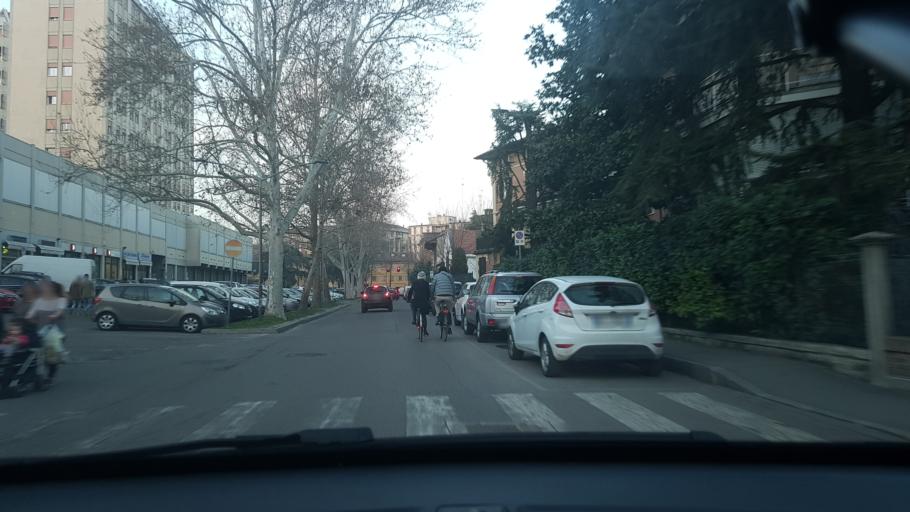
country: IT
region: Emilia-Romagna
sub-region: Provincia di Modena
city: Modena
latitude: 44.6486
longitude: 10.9164
